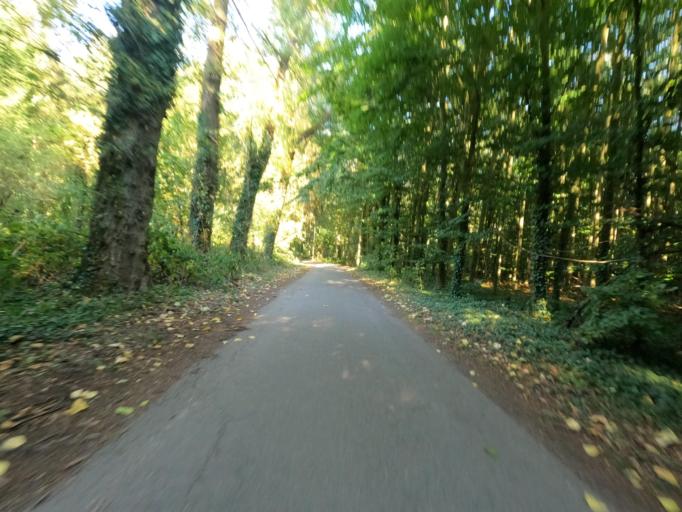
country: NL
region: Limburg
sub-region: Gemeente Roerdalen
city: Vlodrop
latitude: 51.1349
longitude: 6.1078
